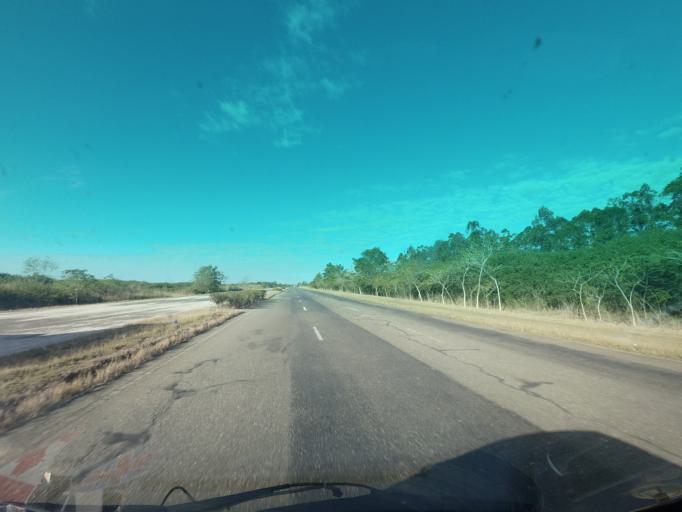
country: CU
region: Cienfuegos
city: Rodas
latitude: 22.4402
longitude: -80.6334
